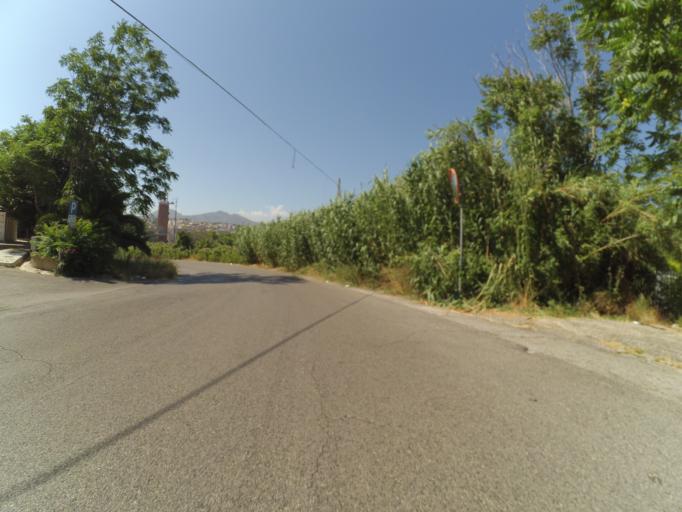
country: IT
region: Latium
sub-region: Provincia di Latina
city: Gaeta
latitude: 41.2123
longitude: 13.5734
